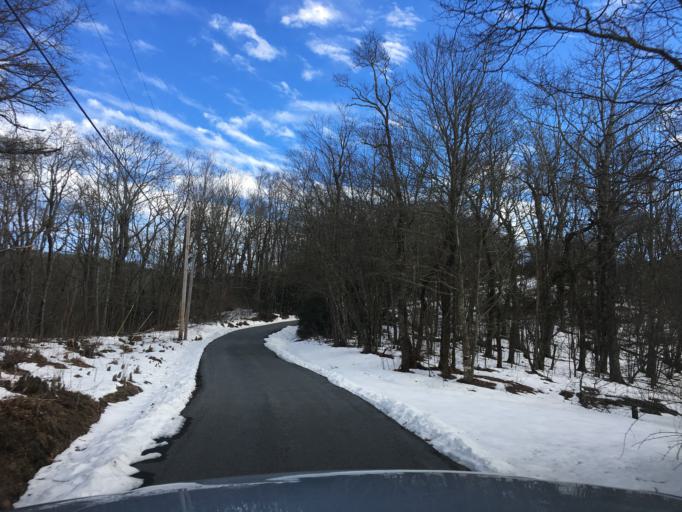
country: US
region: North Carolina
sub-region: Jackson County
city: Cullowhee
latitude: 35.1338
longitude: -82.9896
